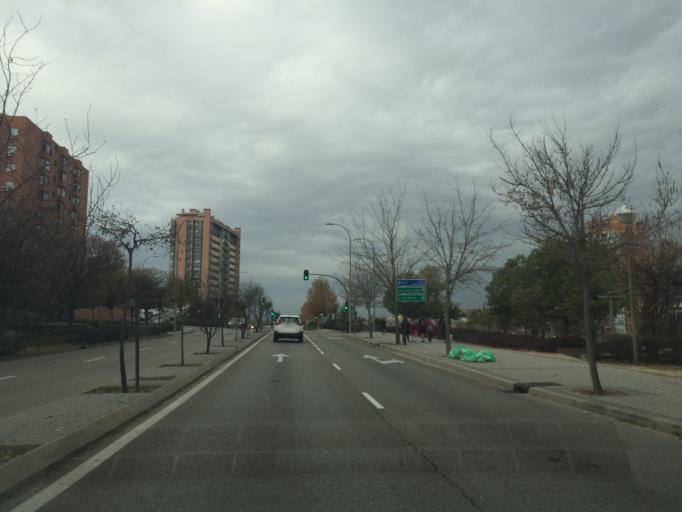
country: ES
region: Madrid
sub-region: Provincia de Madrid
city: Tetuan de las Victorias
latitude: 40.4717
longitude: -3.7217
